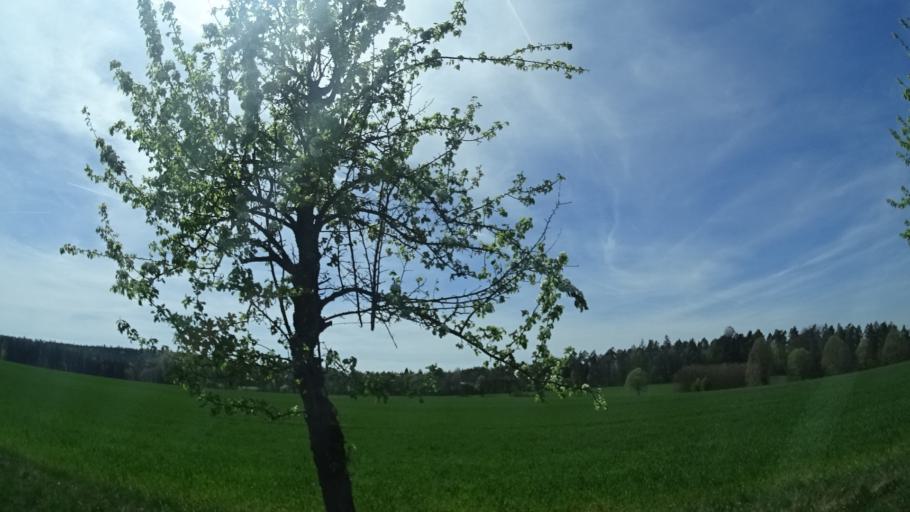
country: DE
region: Bavaria
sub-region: Regierungsbezirk Unterfranken
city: Ermershausen
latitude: 50.1835
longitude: 10.6224
